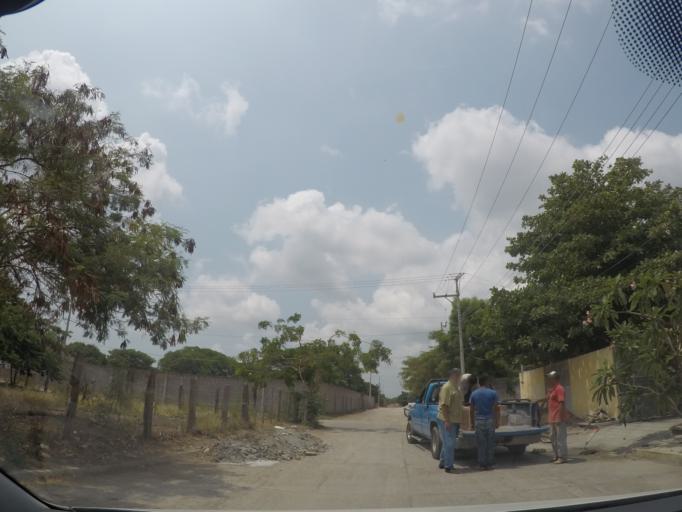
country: MX
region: Oaxaca
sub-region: El Espinal
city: El Espinal
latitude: 16.4776
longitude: -95.0426
